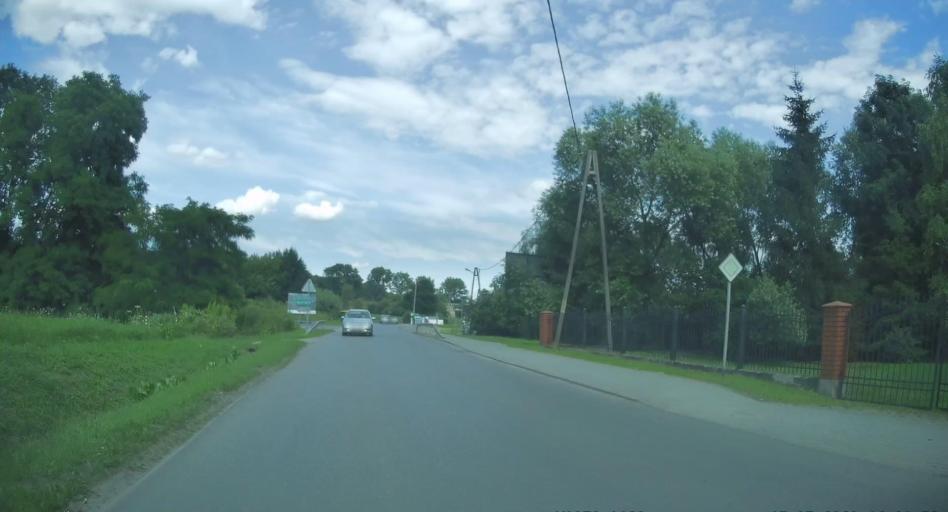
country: PL
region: Subcarpathian Voivodeship
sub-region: Powiat przemyski
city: Zurawica
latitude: 49.8052
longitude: 22.8105
